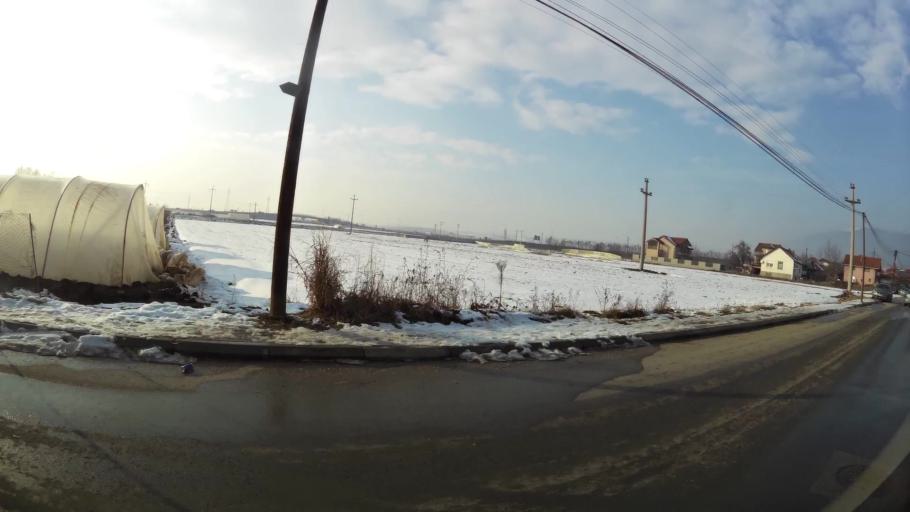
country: MK
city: Creshevo
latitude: 42.0310
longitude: 21.5176
